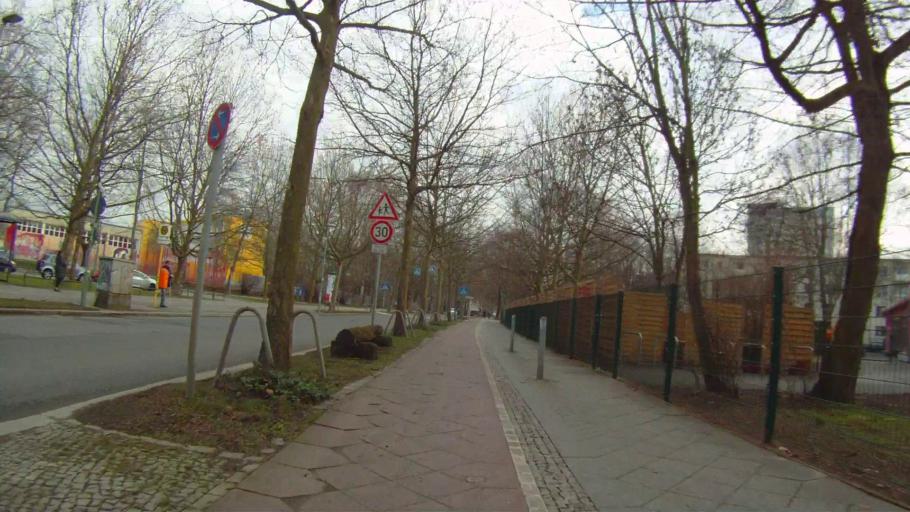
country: DE
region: Berlin
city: Friedrichsfelde
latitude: 52.5020
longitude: 13.5021
